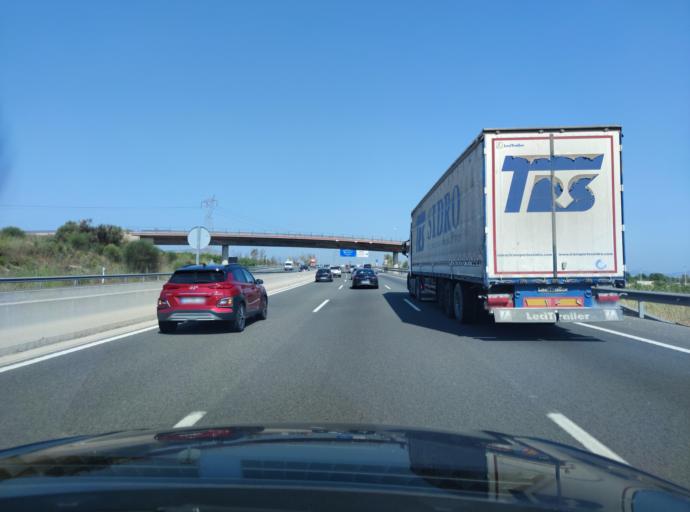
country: ES
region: Valencia
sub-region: Provincia de Valencia
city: Torrent
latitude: 39.4145
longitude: -0.5045
